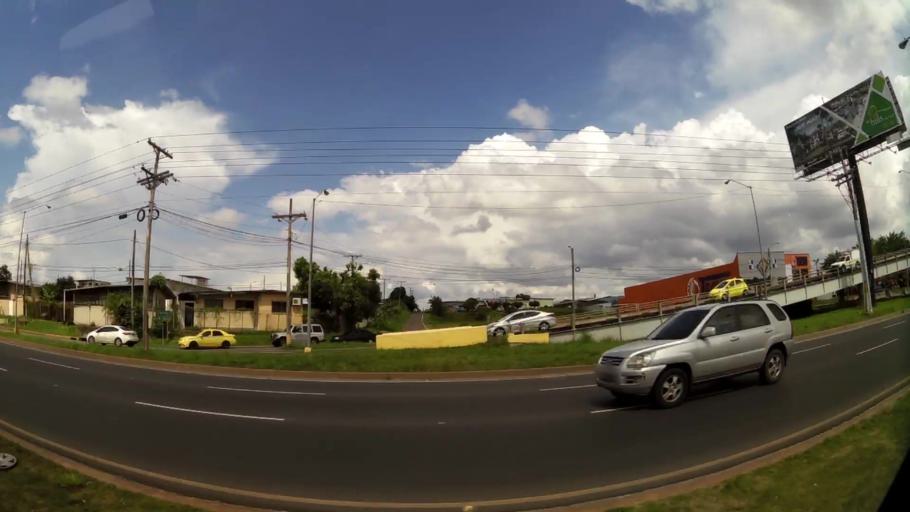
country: PA
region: Panama
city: San Miguelito
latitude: 9.0532
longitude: -79.4417
